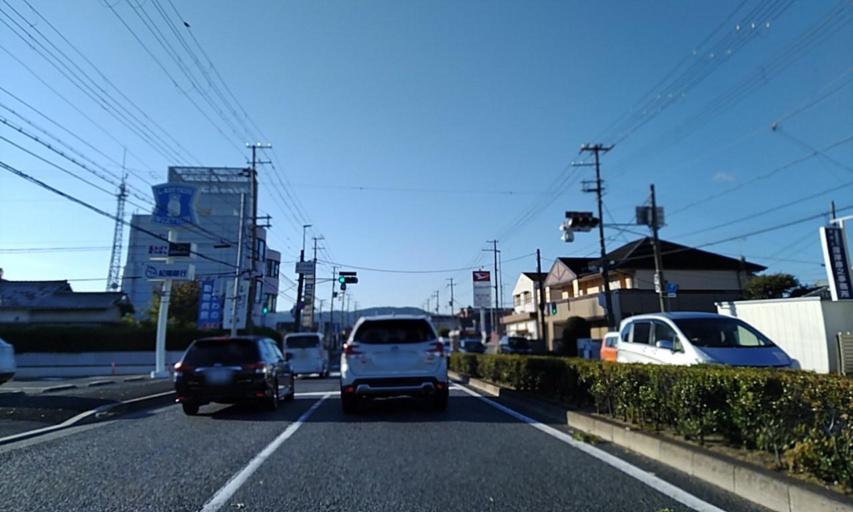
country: JP
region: Wakayama
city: Kainan
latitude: 34.1781
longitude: 135.1864
